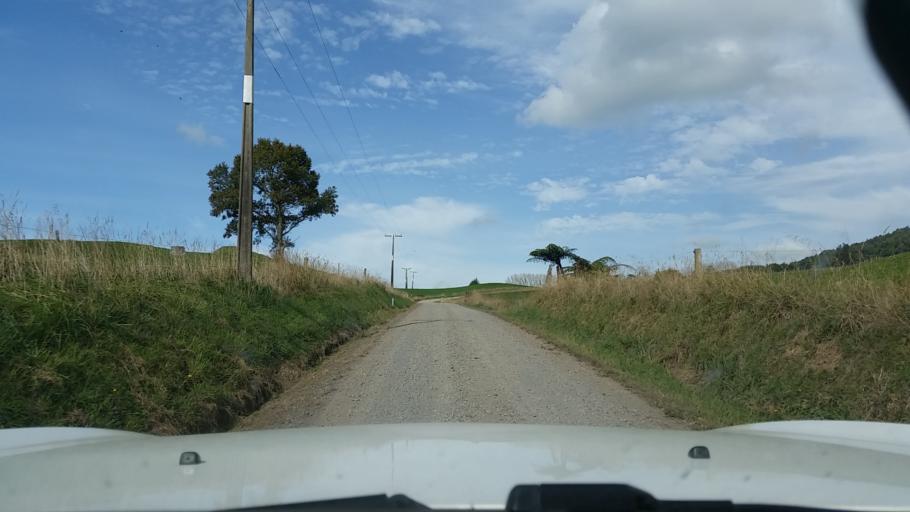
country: NZ
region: Waikato
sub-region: Matamata-Piako District
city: Matamata
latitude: -37.8193
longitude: 175.6751
